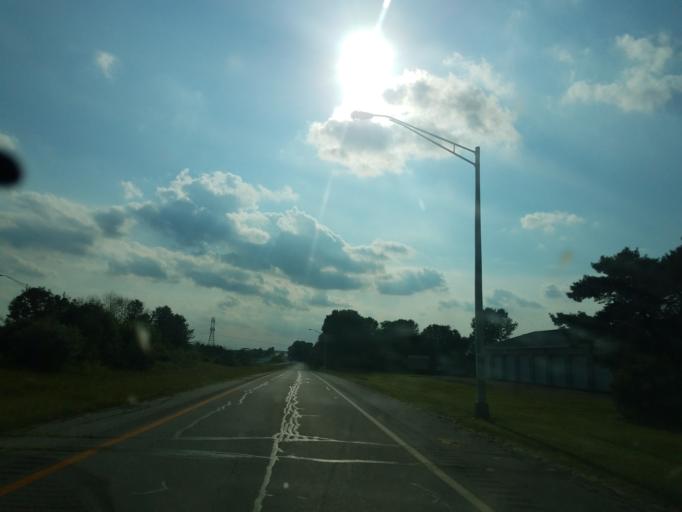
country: US
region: Ohio
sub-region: Wayne County
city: Dalton
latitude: 40.7984
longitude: -81.6504
